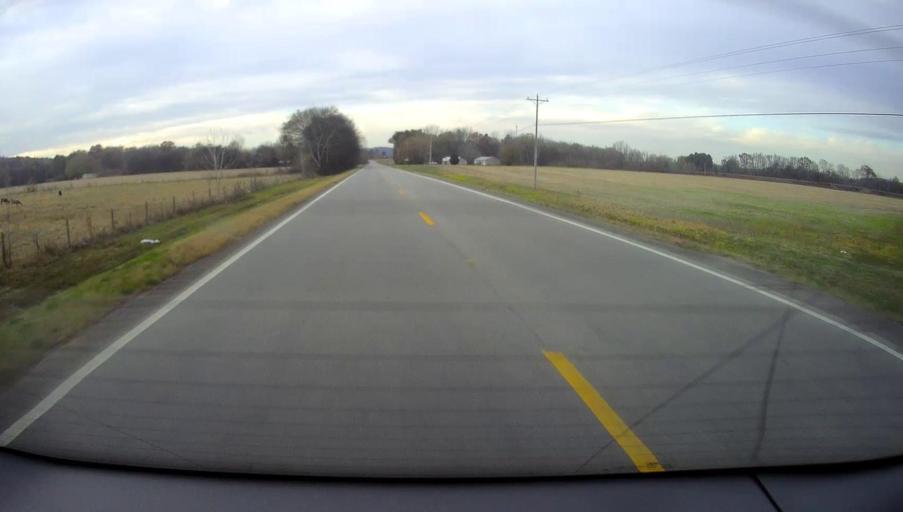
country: US
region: Alabama
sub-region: Marshall County
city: Arab
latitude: 34.4073
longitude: -86.6922
